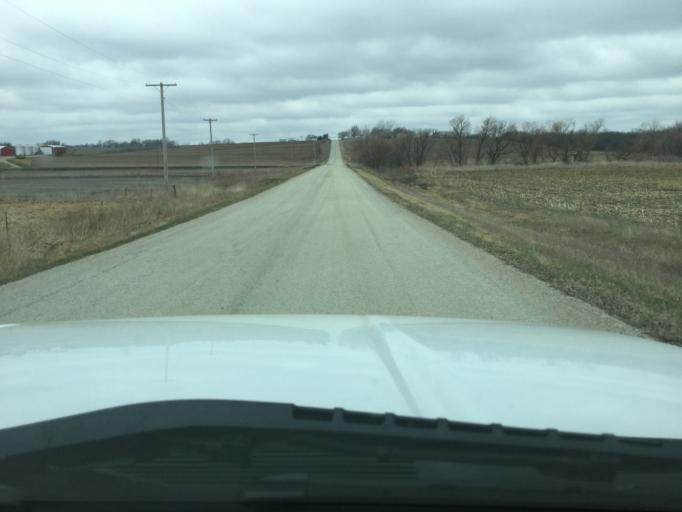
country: US
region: Kansas
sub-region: Nemaha County
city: Seneca
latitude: 39.7399
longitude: -96.0049
